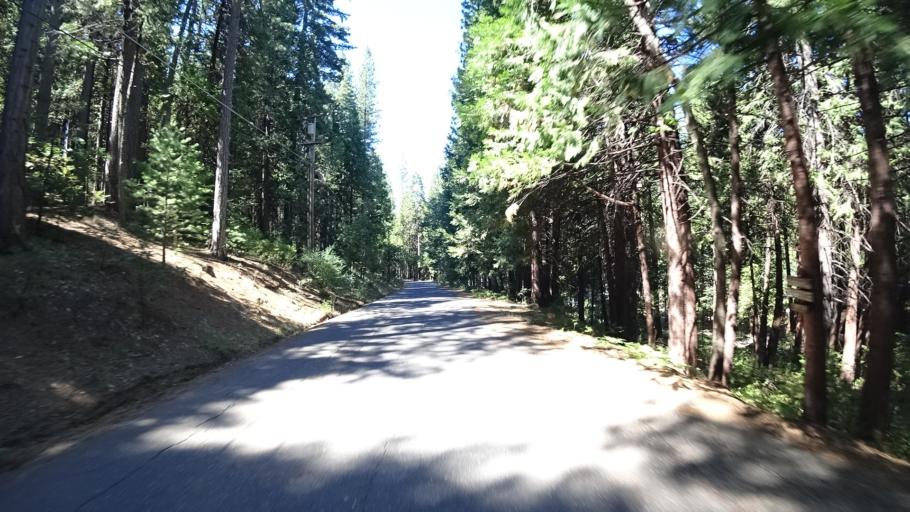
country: US
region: California
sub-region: Calaveras County
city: Arnold
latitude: 38.2408
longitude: -120.3748
